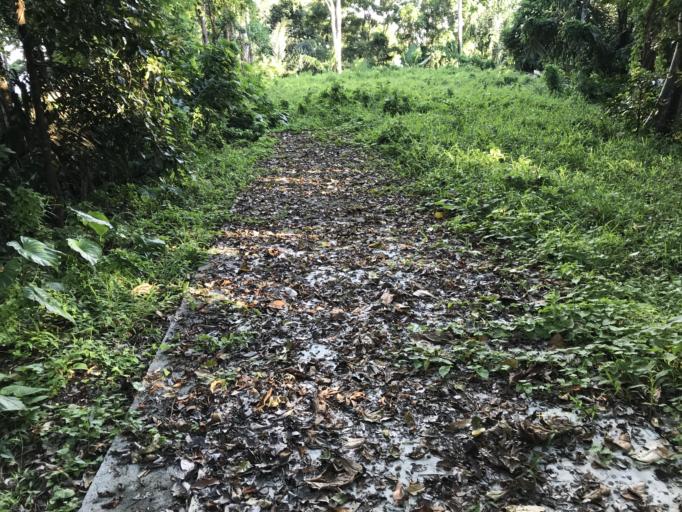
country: ID
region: North Sulawesi
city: Wori
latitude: 1.5640
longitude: 124.8374
